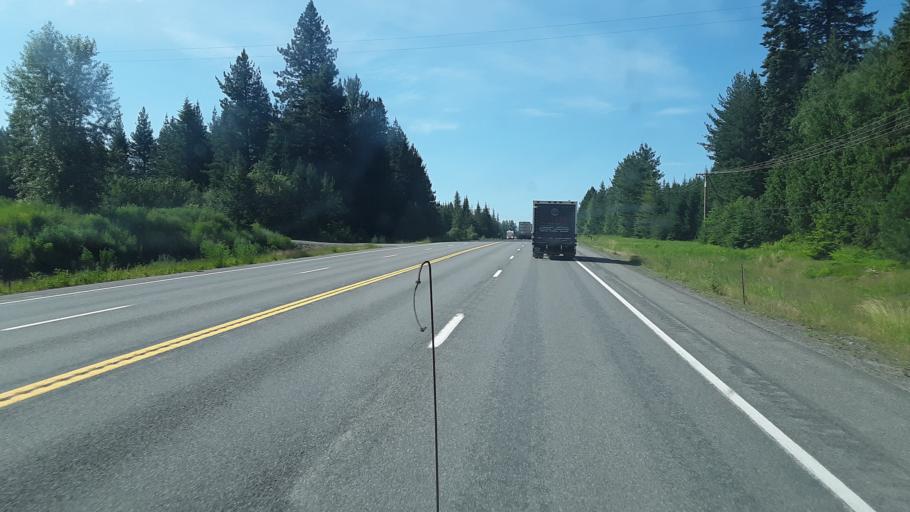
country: US
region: Idaho
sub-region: Bonner County
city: Ponderay
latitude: 48.3403
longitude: -116.5479
